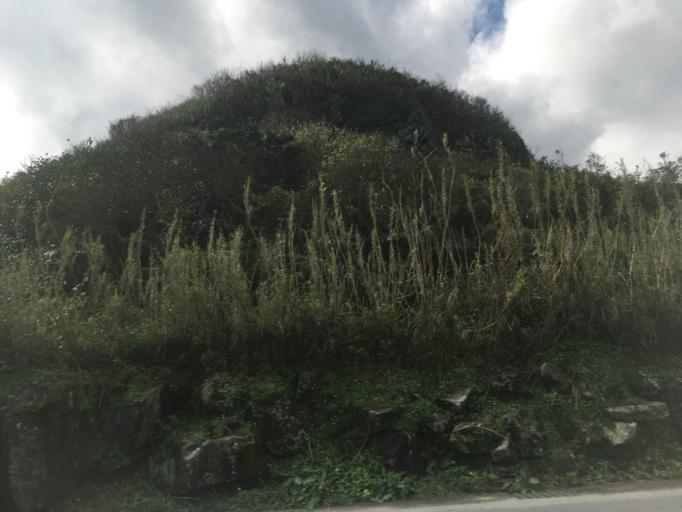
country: TW
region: Taiwan
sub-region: Keelung
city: Keelung
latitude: 25.0204
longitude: 121.9554
